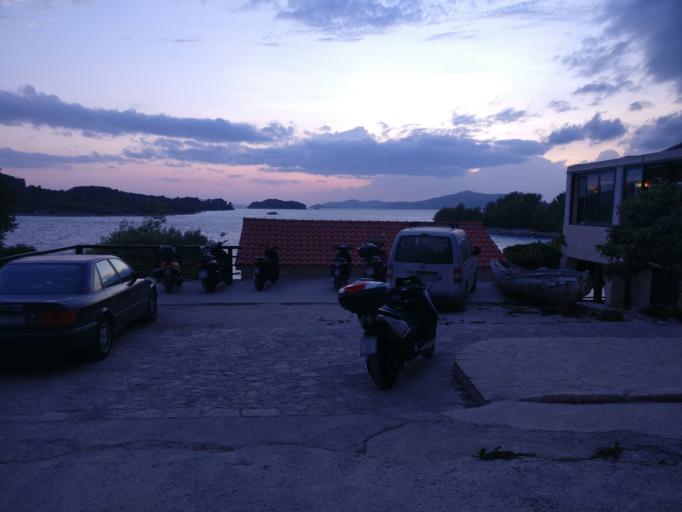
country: HR
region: Splitsko-Dalmatinska
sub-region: Grad Trogir
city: Trogir
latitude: 43.4815
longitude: 16.2423
